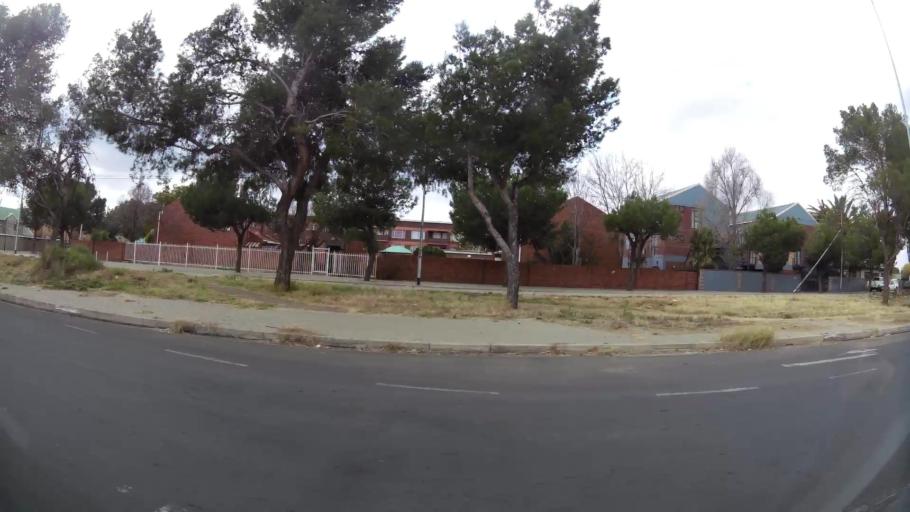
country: ZA
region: Orange Free State
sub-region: Mangaung Metropolitan Municipality
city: Bloemfontein
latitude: -29.1205
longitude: 26.1992
